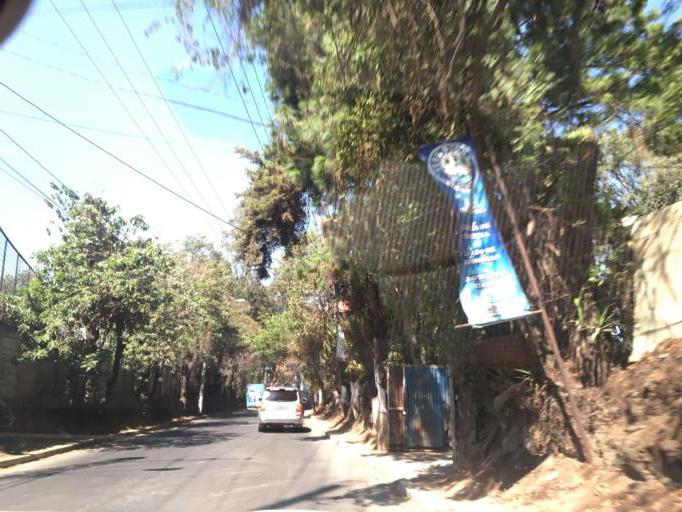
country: GT
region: Guatemala
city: Mixco
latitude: 14.6225
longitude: -90.6027
